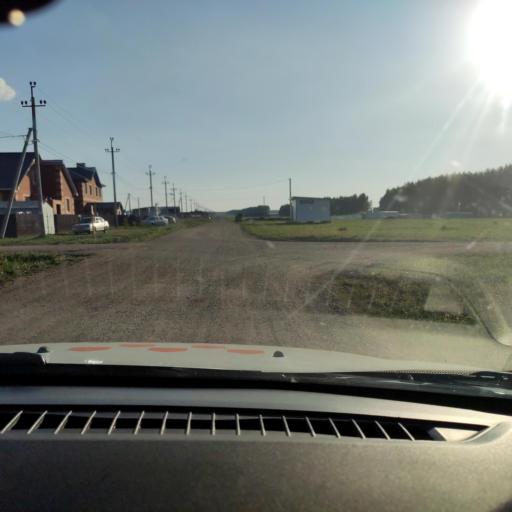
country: RU
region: Bashkortostan
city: Karmaskaly
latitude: 54.3532
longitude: 56.1446
